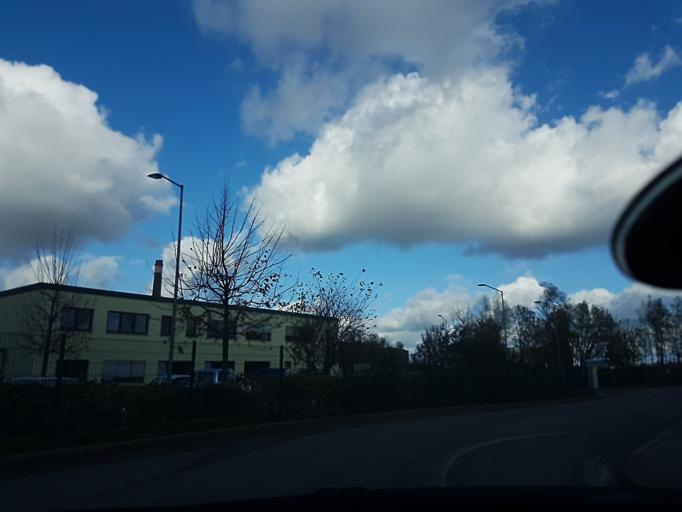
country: DE
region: Saxony
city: Freiberg
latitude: 50.9043
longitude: 13.3670
